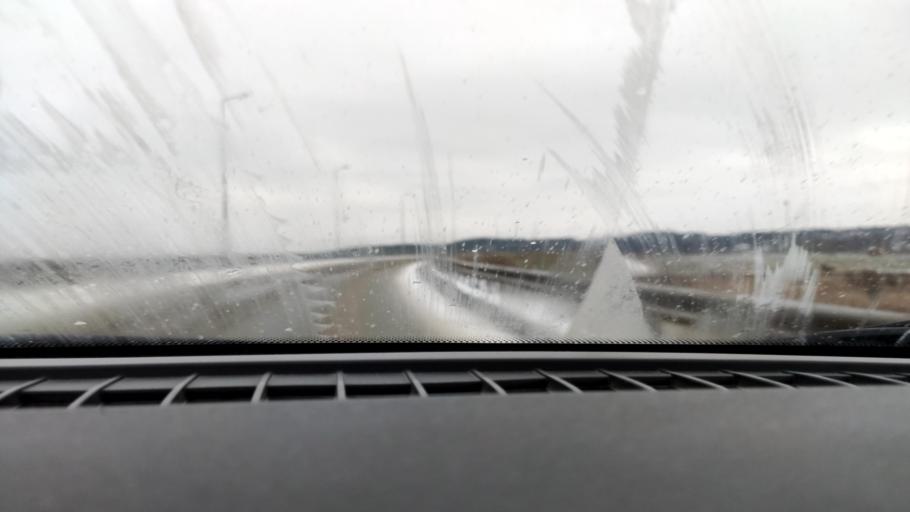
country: RU
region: Perm
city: Kondratovo
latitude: 57.9268
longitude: 56.1730
